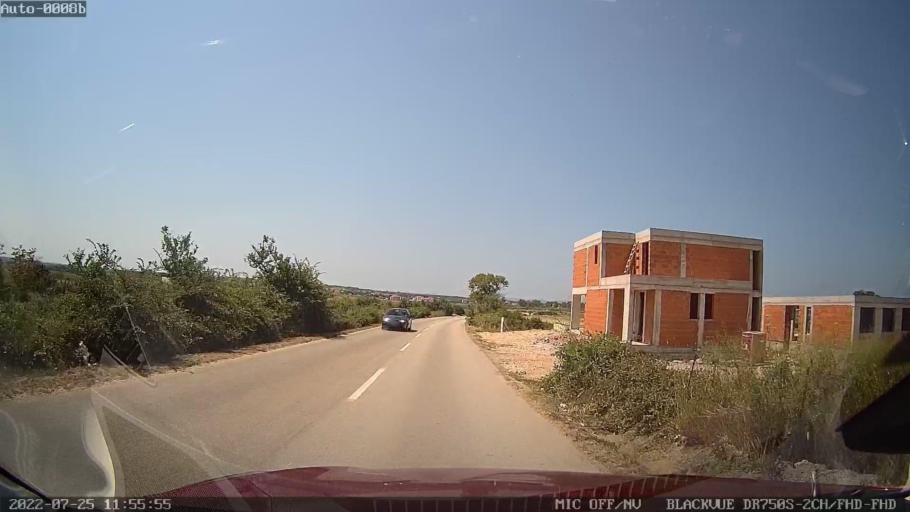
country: HR
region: Zadarska
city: Vrsi
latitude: 44.2535
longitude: 15.2223
